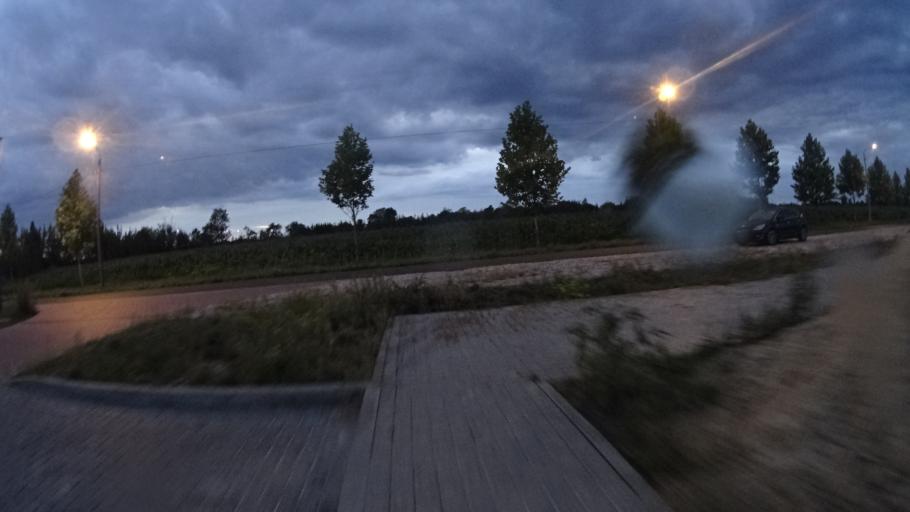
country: PL
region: Masovian Voivodeship
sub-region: Powiat warszawski zachodni
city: Ozarow Mazowiecki
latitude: 52.2313
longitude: 20.7971
